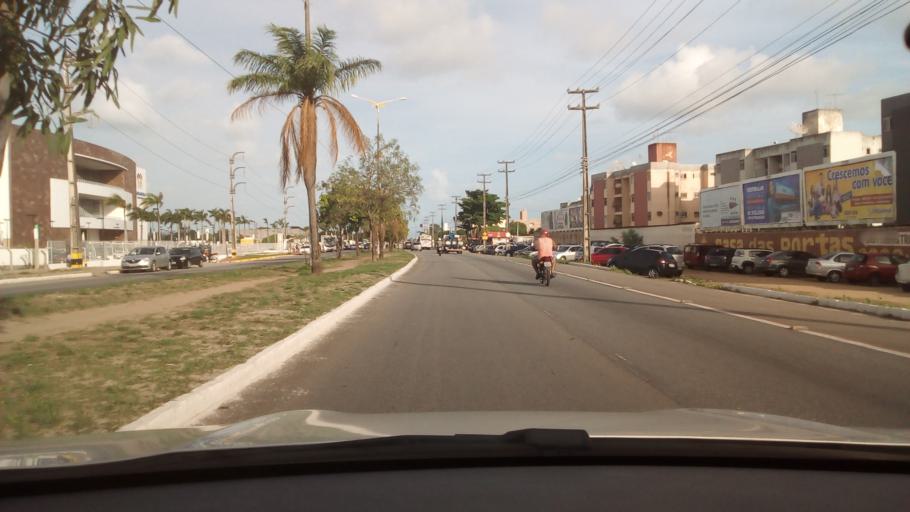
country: BR
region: Paraiba
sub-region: Joao Pessoa
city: Joao Pessoa
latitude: -7.1631
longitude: -34.8326
